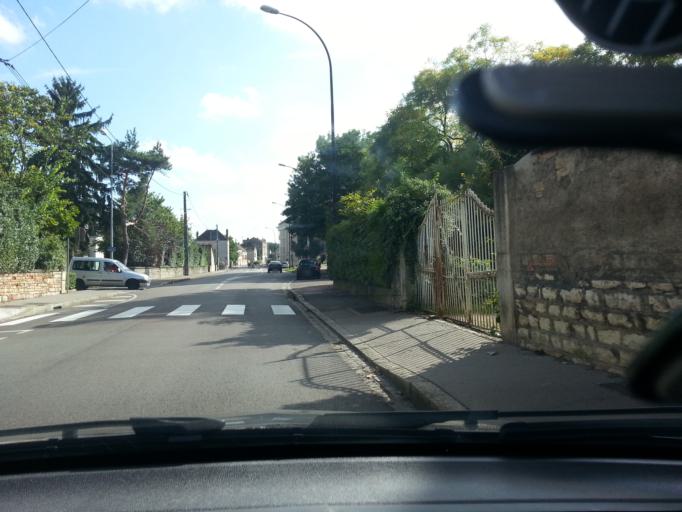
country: FR
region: Bourgogne
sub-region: Departement de Saone-et-Loire
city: Chalon-sur-Saone
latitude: 46.7975
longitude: 4.8583
